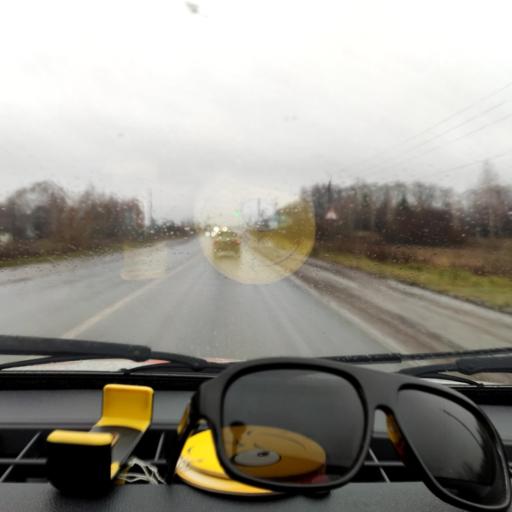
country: RU
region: Bashkortostan
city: Iglino
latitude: 54.7947
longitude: 56.2632
